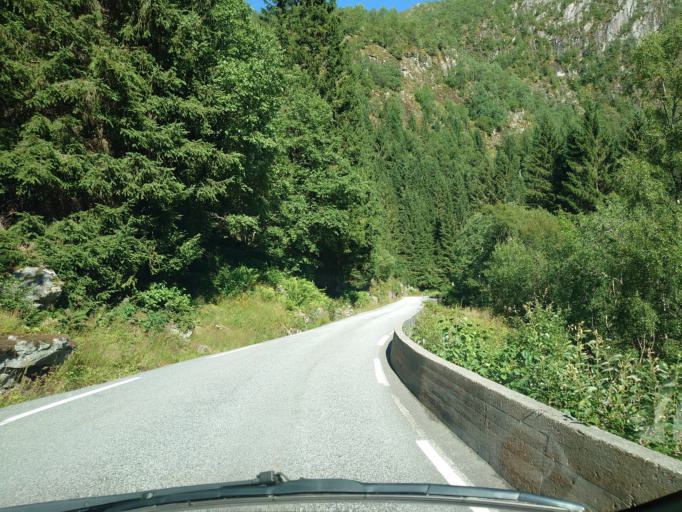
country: NO
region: Hordaland
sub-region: Vaksdal
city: Dale
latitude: 60.5873
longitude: 5.8517
